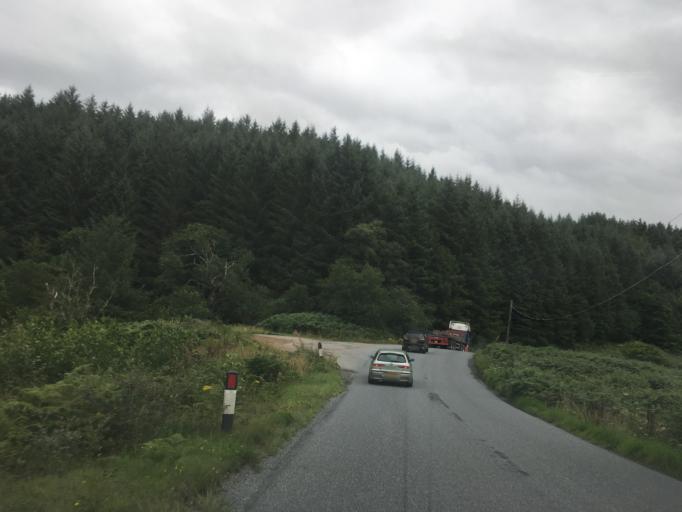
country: GB
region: Scotland
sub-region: Argyll and Bute
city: Oban
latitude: 56.2752
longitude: -5.4784
